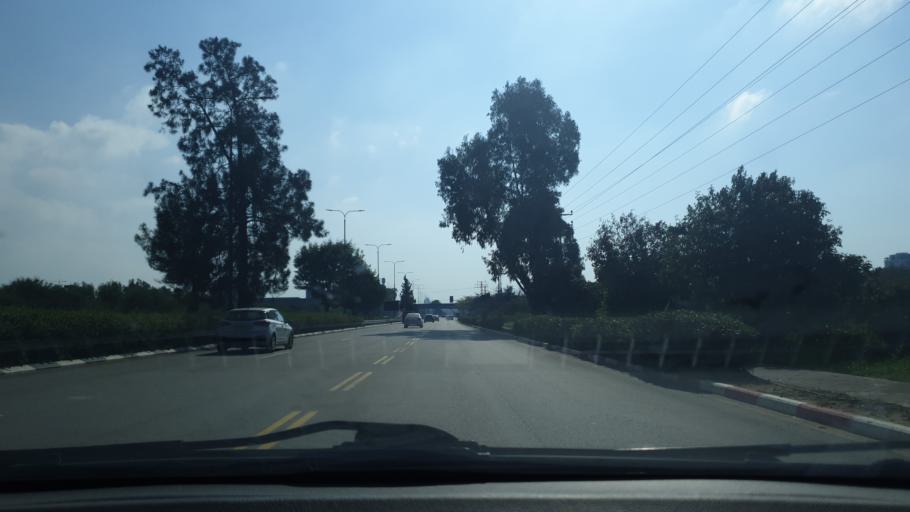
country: IL
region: Central District
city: Bet Dagan
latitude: 31.9881
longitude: 34.8117
